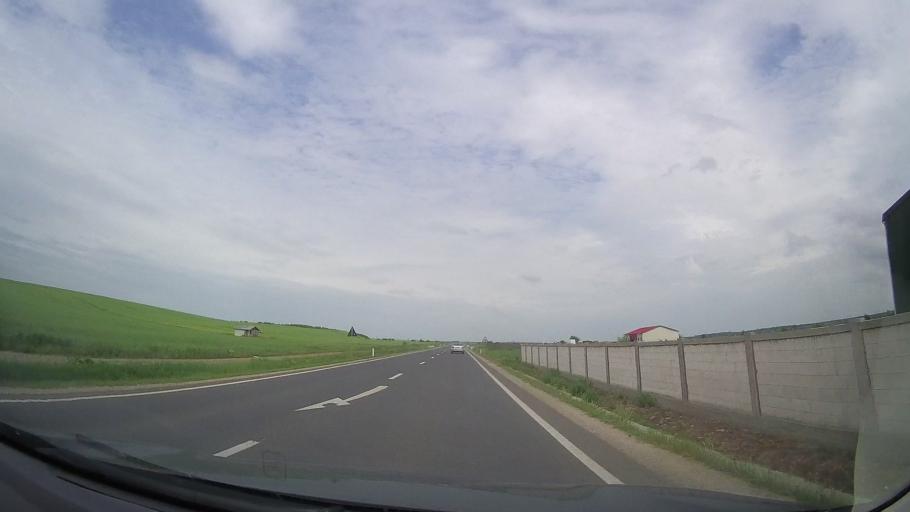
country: RO
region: Teleorman
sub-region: Comuna Peretu
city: Peretu
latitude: 44.0541
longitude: 25.0571
